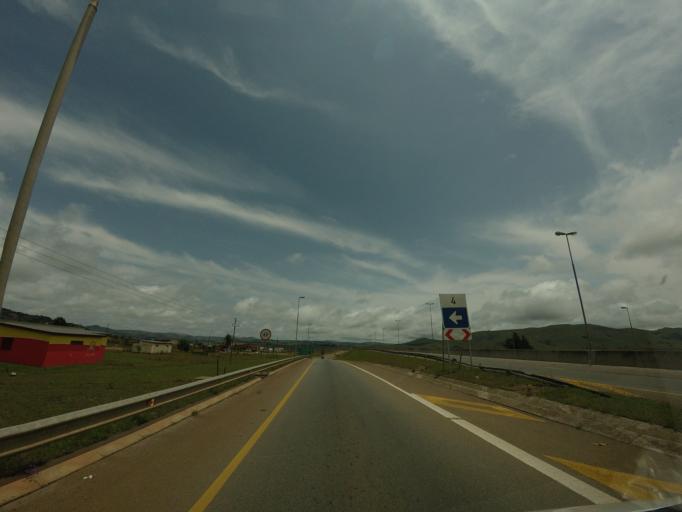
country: SZ
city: Darkton
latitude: -26.2442
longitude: 31.0558
